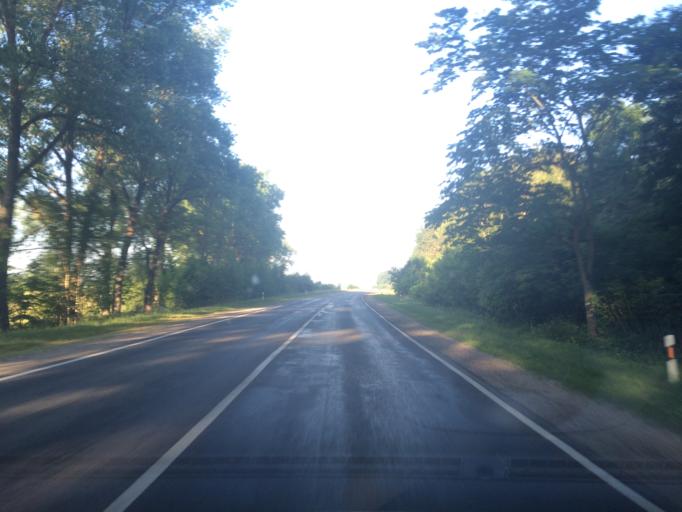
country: LT
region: Utenos apskritis
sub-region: Anyksciai
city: Anyksciai
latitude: 55.3678
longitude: 25.0074
